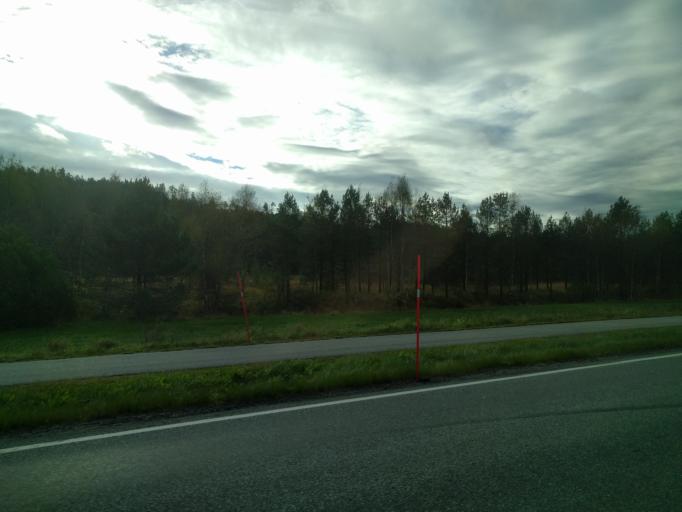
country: NO
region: Vest-Agder
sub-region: Songdalen
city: Nodeland
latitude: 58.2746
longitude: 7.8325
